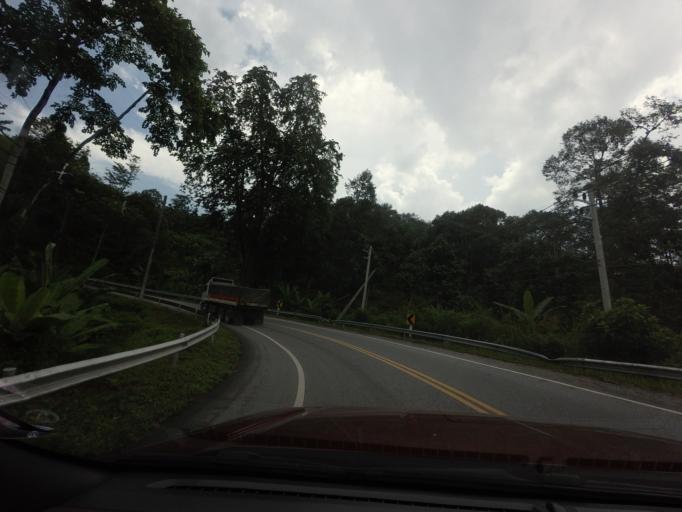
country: TH
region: Yala
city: Than To
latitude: 6.0877
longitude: 101.1821
